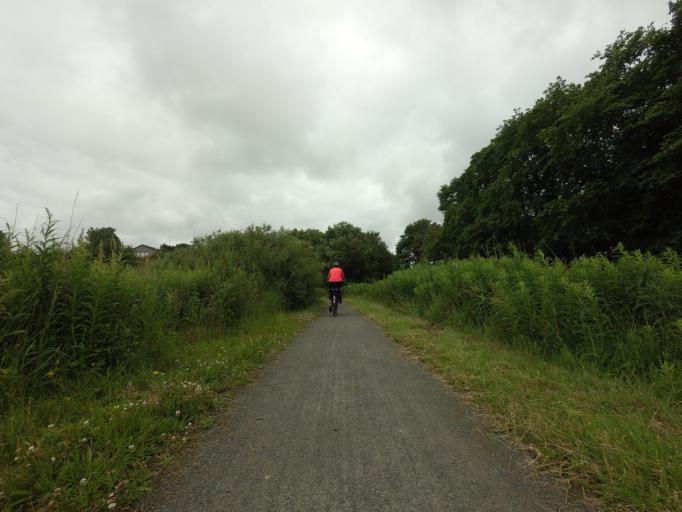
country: GB
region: Scotland
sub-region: Aberdeenshire
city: Ellon
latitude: 57.4772
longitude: -2.1293
